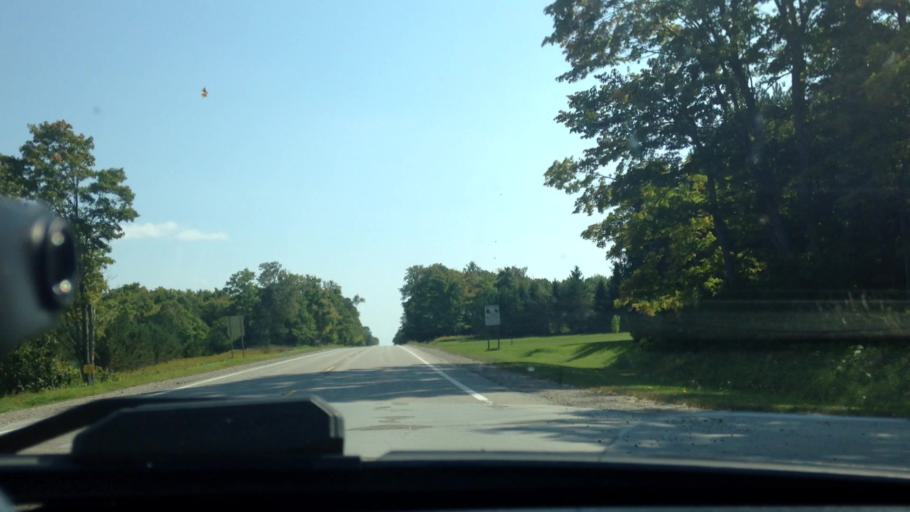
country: US
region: Michigan
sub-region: Luce County
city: Newberry
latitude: 46.3248
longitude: -85.6710
